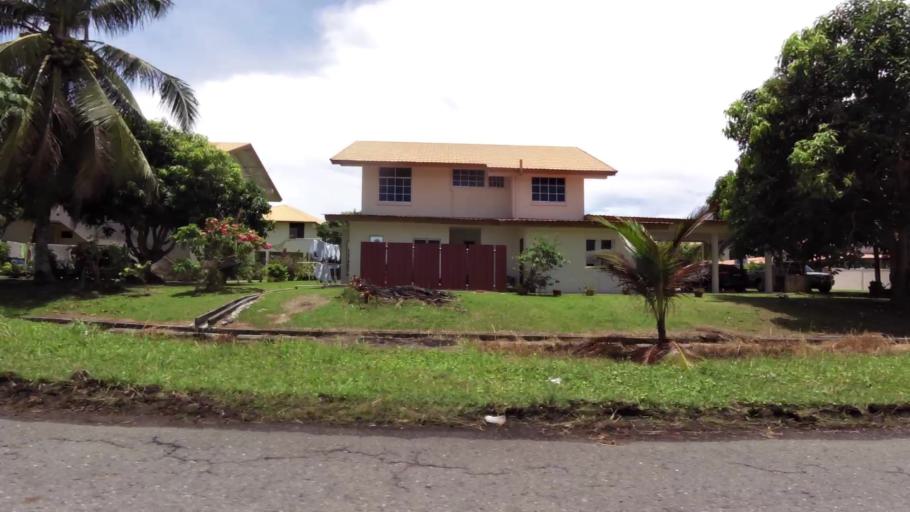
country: BN
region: Belait
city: Kuala Belait
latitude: 4.5902
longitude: 114.2492
